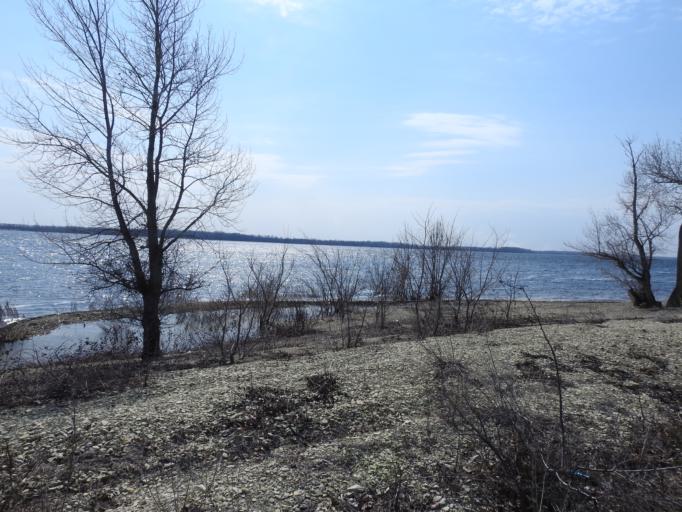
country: RU
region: Saratov
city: Voskresenskoye
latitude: 51.7953
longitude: 46.8715
